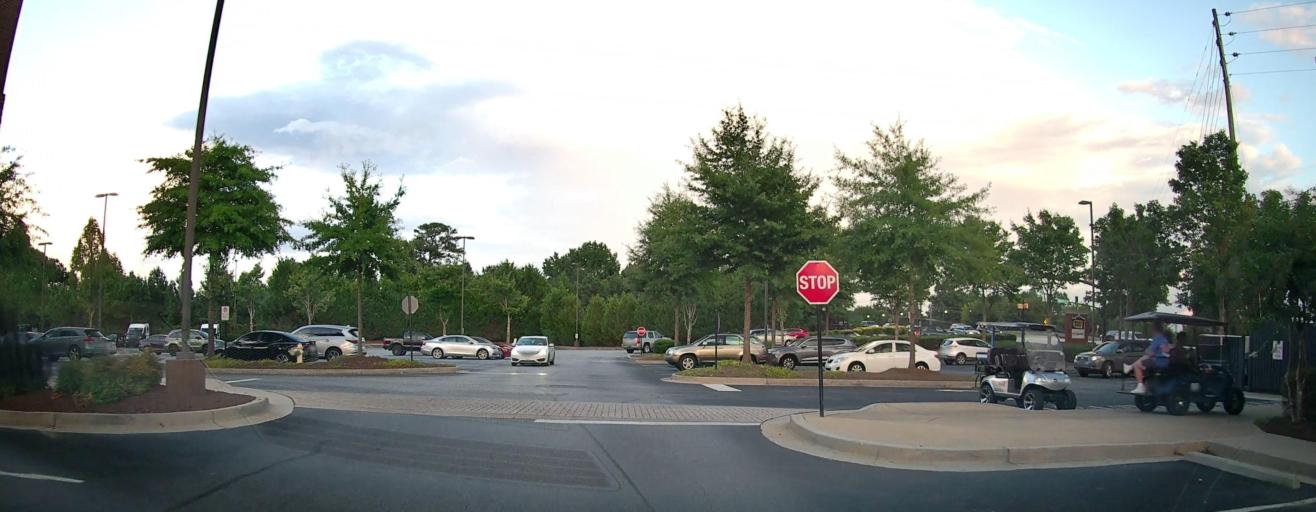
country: US
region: Georgia
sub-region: Fayette County
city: Peachtree City
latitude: 33.3973
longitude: -84.5971
